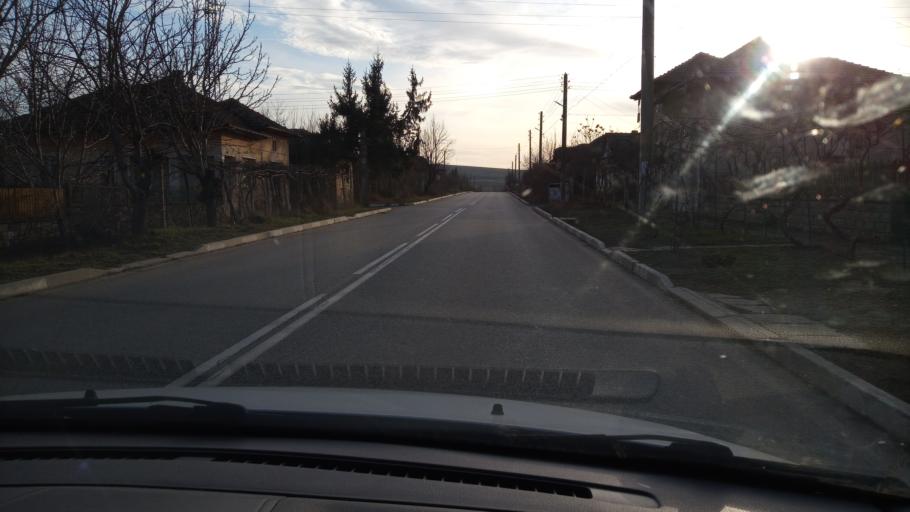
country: BG
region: Pleven
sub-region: Obshtina Pleven
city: Slavyanovo
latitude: 43.5511
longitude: 24.8637
